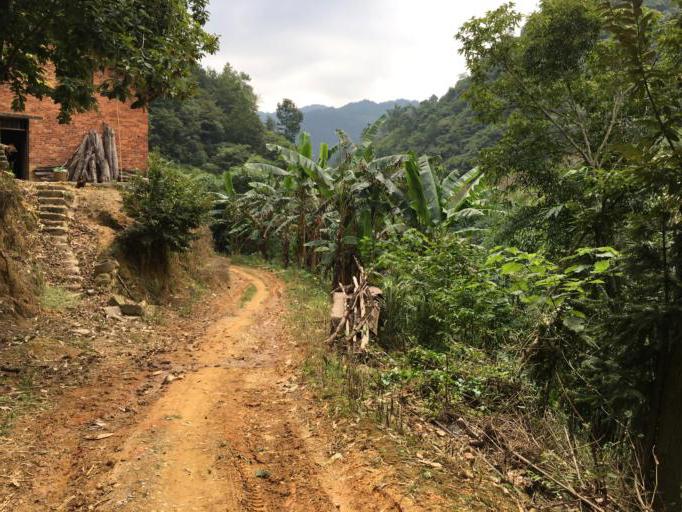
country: CN
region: Guangxi Zhuangzu Zizhiqu
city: Tongle
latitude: 25.2991
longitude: 106.1413
